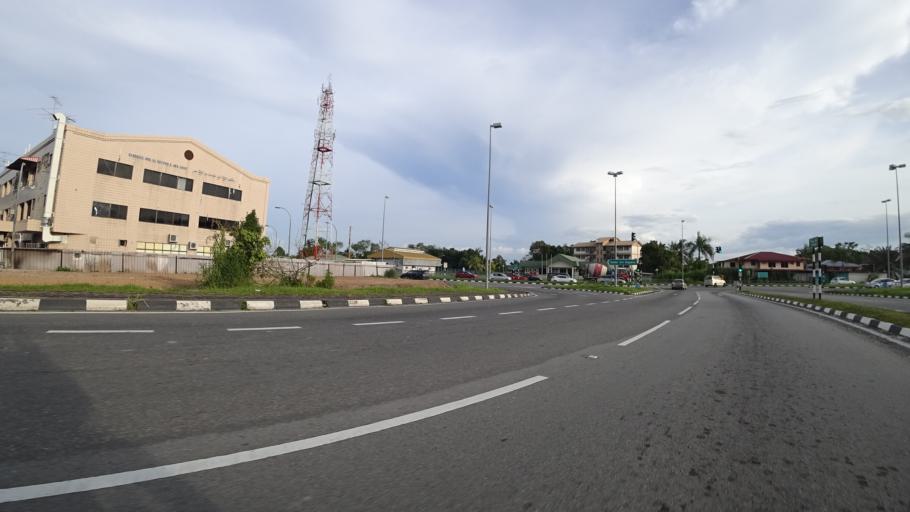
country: BN
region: Brunei and Muara
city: Bandar Seri Begawan
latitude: 4.8862
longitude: 114.8387
